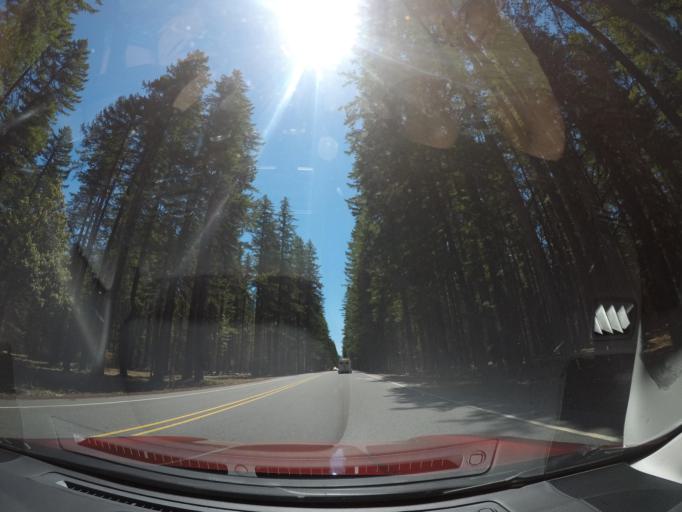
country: US
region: Oregon
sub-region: Linn County
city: Mill City
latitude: 44.6832
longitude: -121.9688
